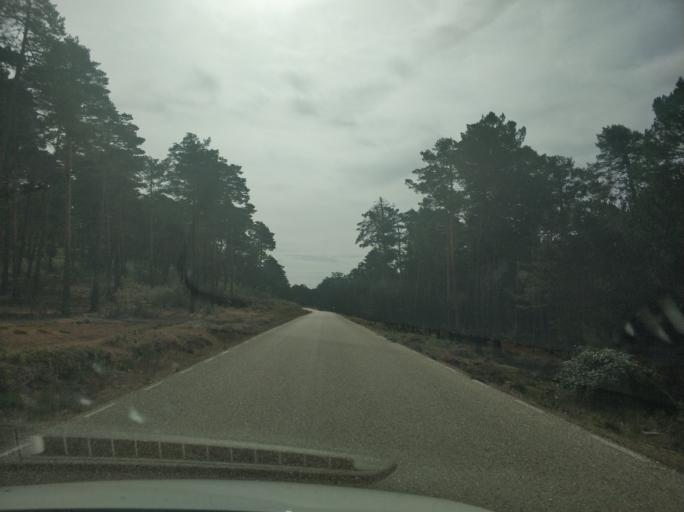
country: ES
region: Castille and Leon
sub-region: Provincia de Soria
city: Navaleno
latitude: 41.8563
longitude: -2.9677
